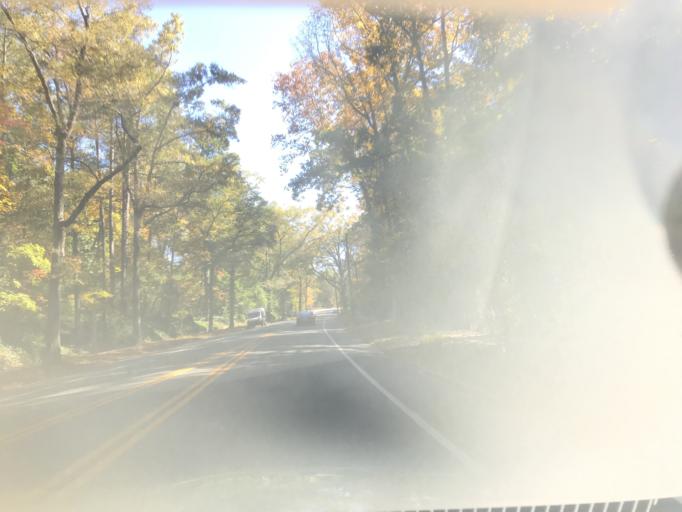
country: US
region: North Carolina
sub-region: Durham County
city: Durham
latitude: 35.9980
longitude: -78.9272
